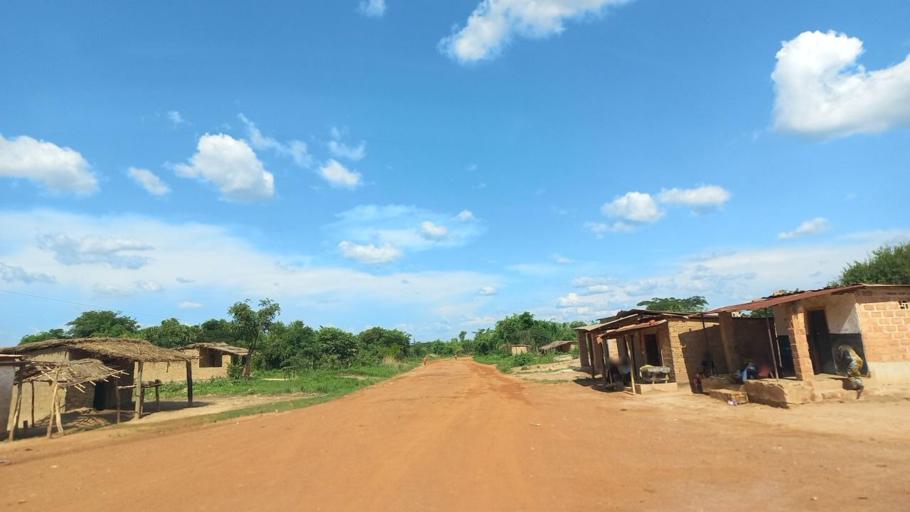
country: ZM
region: Copperbelt
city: Kitwe
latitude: -12.8656
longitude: 28.3718
